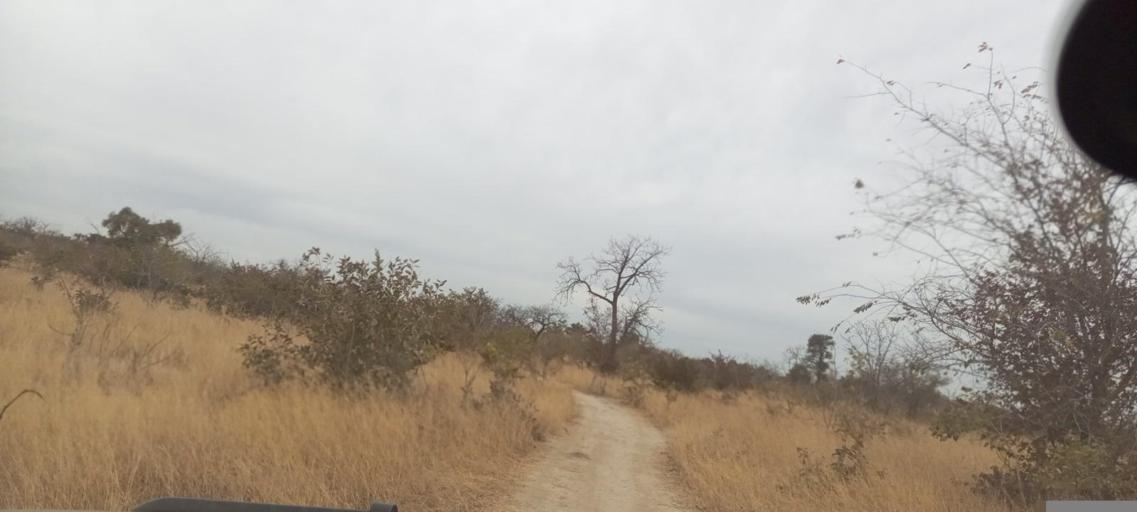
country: ML
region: Koulikoro
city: Kati
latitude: 12.7712
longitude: -8.3778
